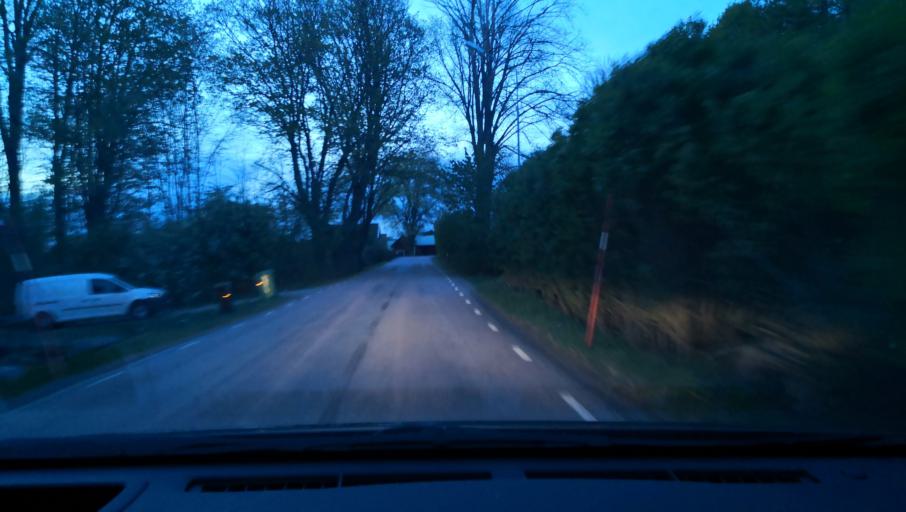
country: SE
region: OErebro
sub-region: Askersunds Kommun
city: Asbro
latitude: 59.0716
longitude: 15.0042
